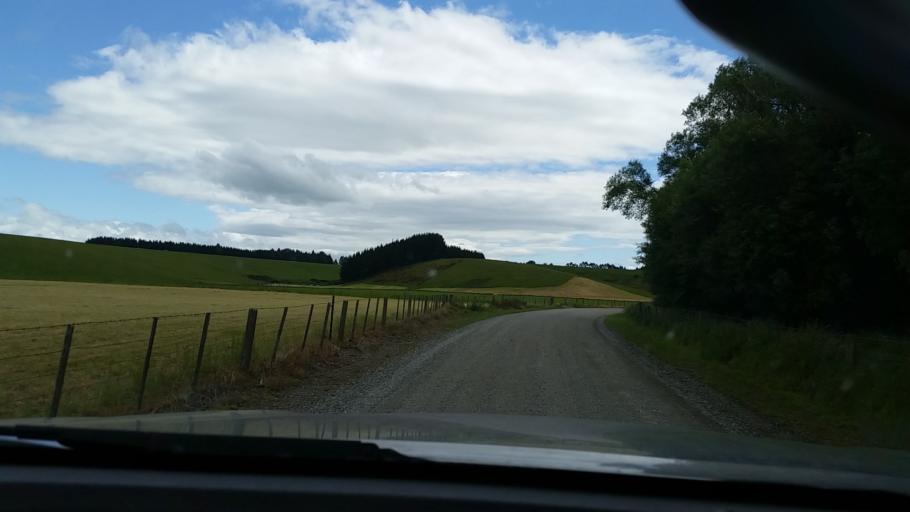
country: NZ
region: Otago
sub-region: Queenstown-Lakes District
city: Kingston
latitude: -45.7654
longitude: 168.6195
